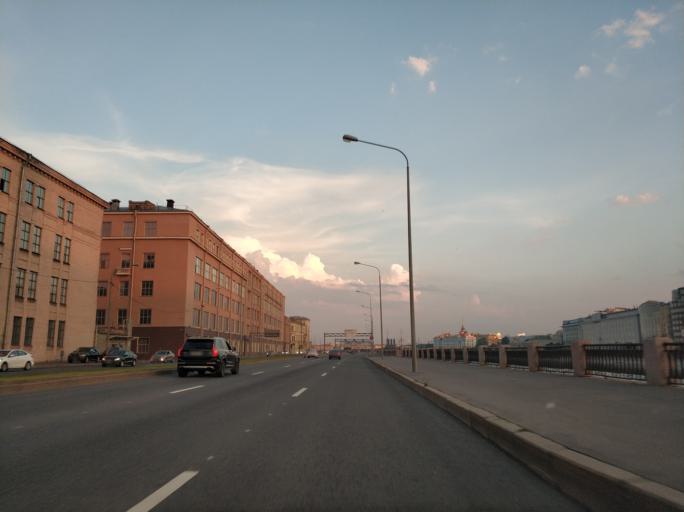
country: RU
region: Leningrad
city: Sampsonievskiy
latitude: 59.9635
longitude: 30.3376
